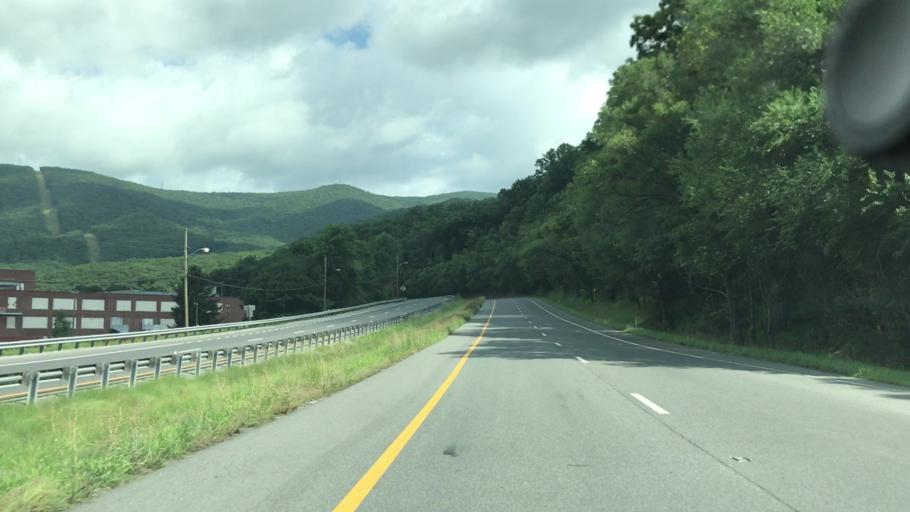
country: US
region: Virginia
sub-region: Giles County
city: Pearisburg
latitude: 37.3437
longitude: -80.7593
